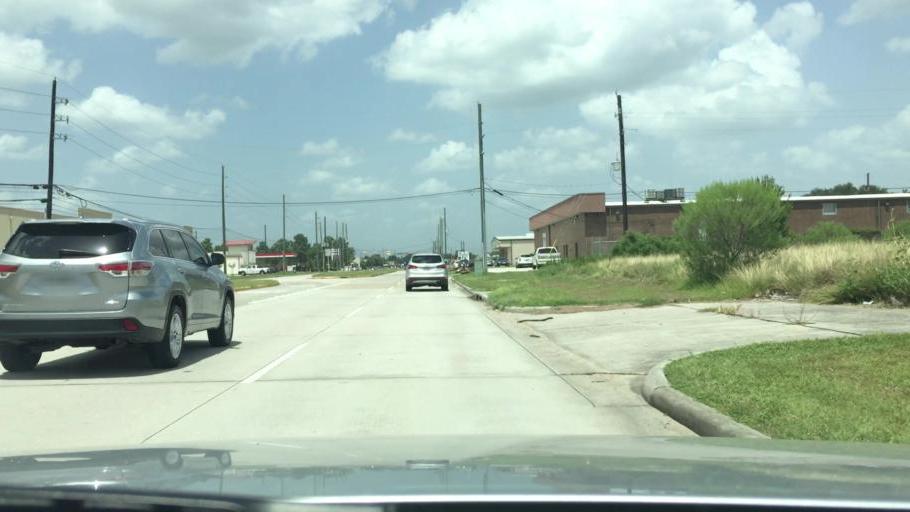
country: US
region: Texas
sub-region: Harris County
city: Hudson
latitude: 29.9538
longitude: -95.5229
